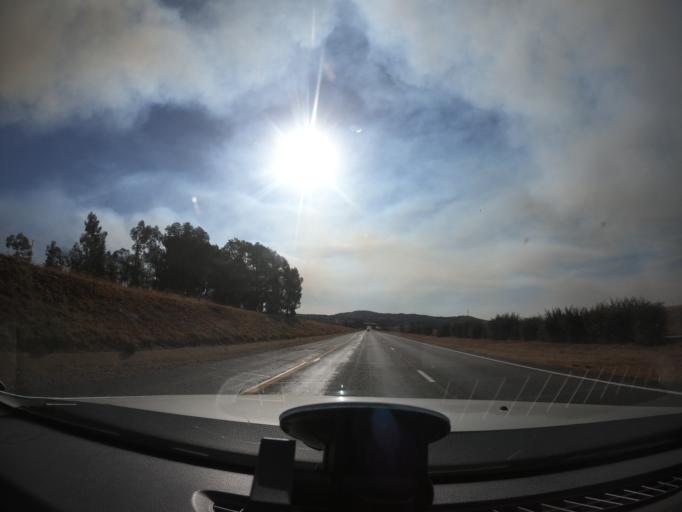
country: ZA
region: Gauteng
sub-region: Sedibeng District Municipality
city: Heidelberg
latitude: -26.5068
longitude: 28.3845
